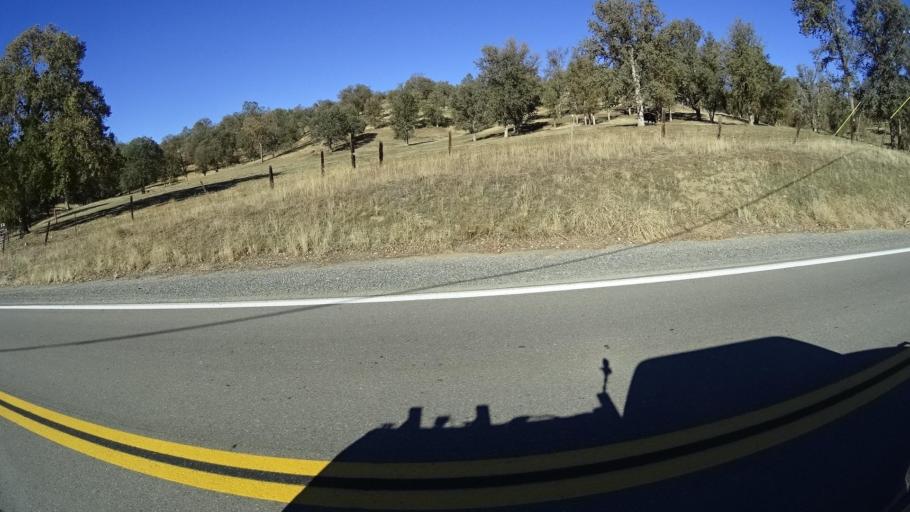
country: US
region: California
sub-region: Kern County
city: Alta Sierra
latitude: 35.7181
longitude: -118.7268
